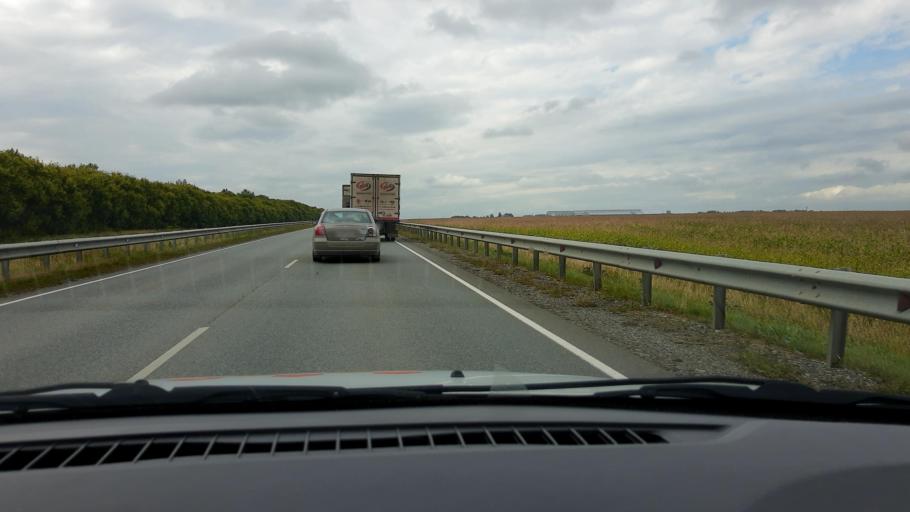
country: RU
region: Tatarstan
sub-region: Alekseyevskiy Rayon
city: Alekseyevskoye
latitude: 55.3141
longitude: 50.2592
